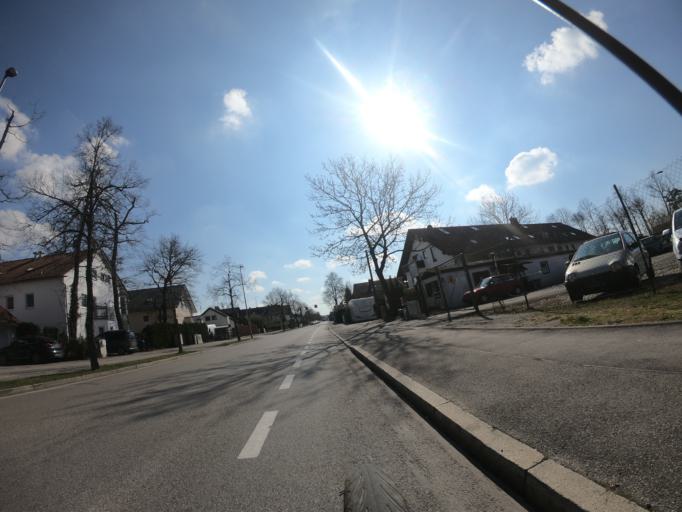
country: DE
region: Bavaria
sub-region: Upper Bavaria
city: Fuerstenfeldbruck
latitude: 48.1915
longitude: 11.2561
